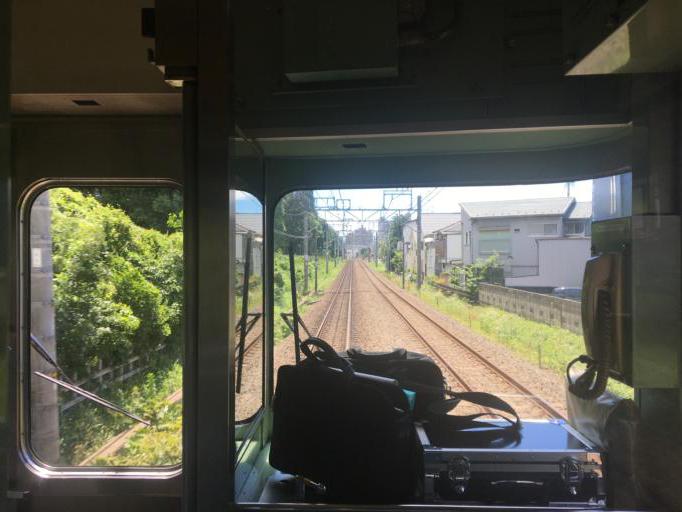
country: JP
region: Tokyo
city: Higashimurayama-shi
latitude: 35.7410
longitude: 139.4827
